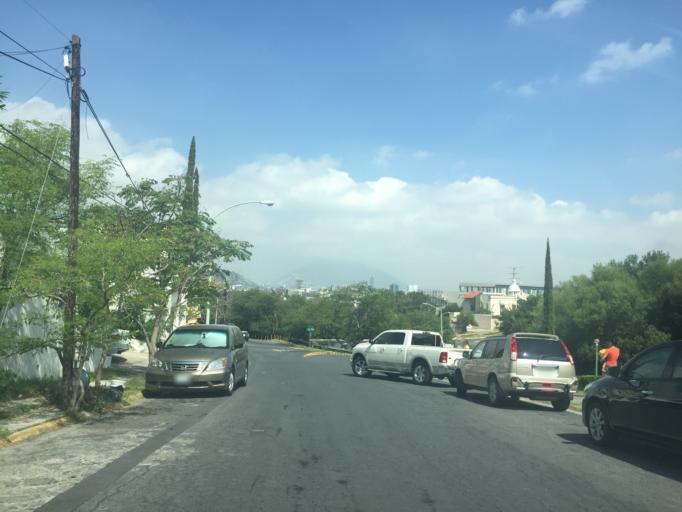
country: MX
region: Nuevo Leon
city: Guadalupe
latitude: 25.6387
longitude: -100.2662
